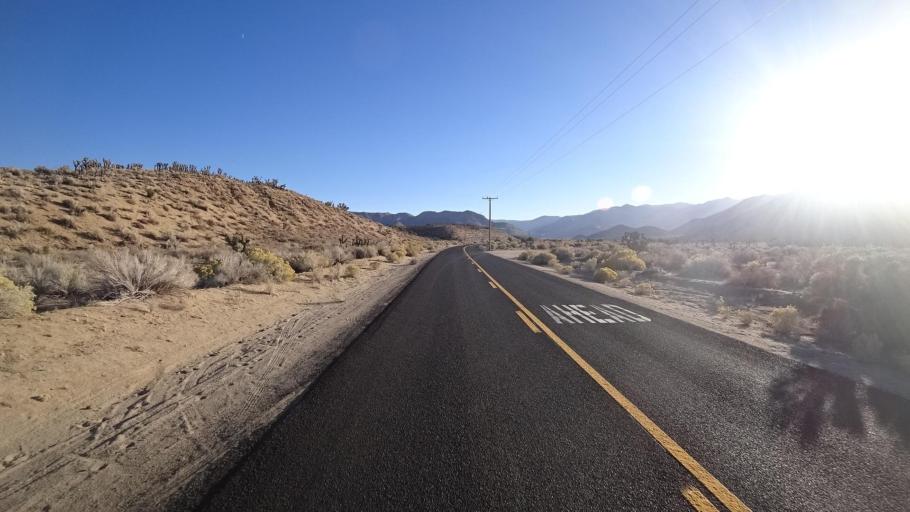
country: US
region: California
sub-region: Kern County
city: Weldon
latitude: 35.6123
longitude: -118.2430
